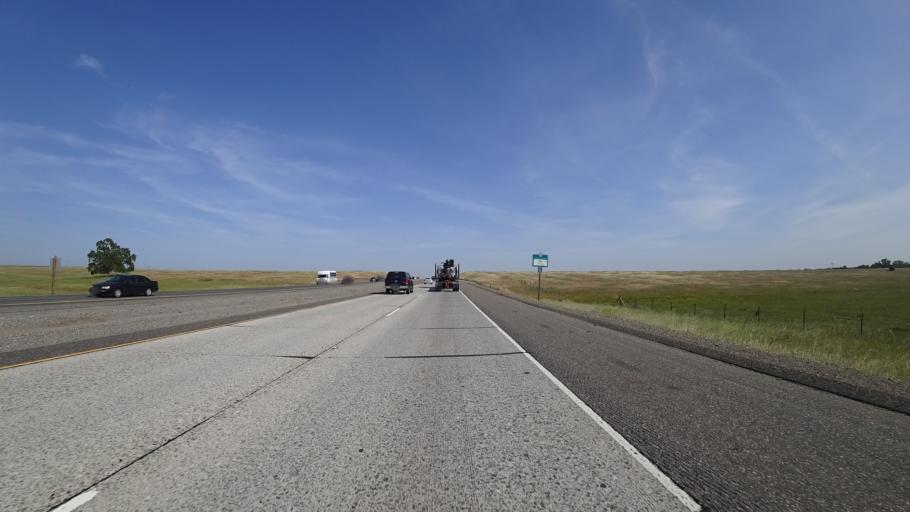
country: US
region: California
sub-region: Butte County
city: Durham
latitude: 39.6791
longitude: -121.7614
